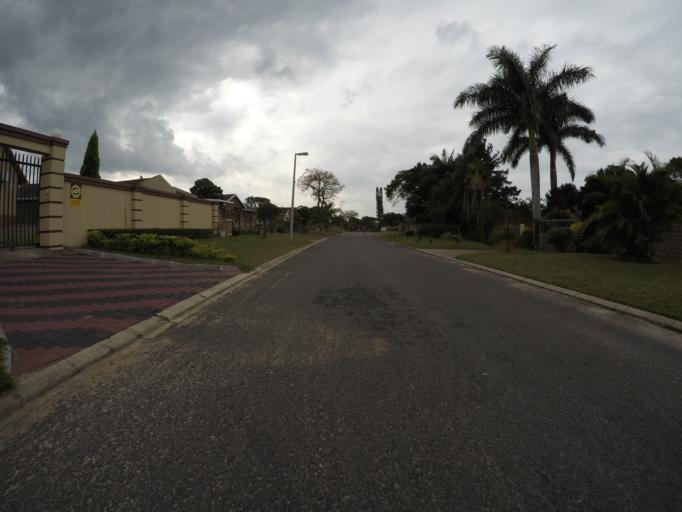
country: ZA
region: KwaZulu-Natal
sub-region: uThungulu District Municipality
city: Richards Bay
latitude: -28.7374
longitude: 32.0523
